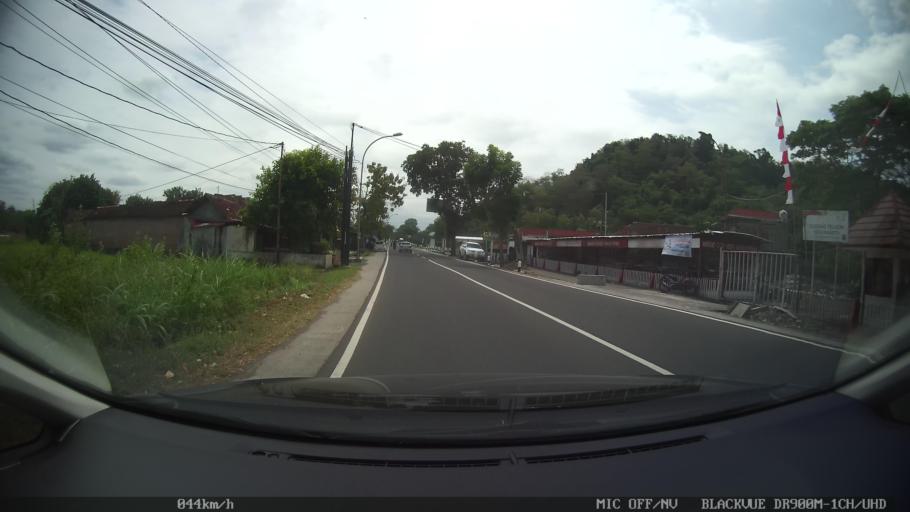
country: ID
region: Central Java
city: Candi Prambanan
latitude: -7.7764
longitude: 110.4826
